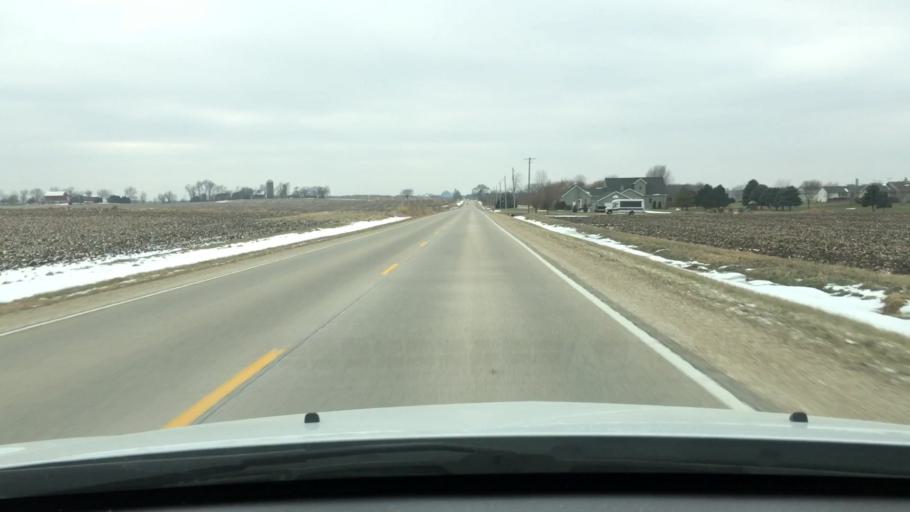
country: US
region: Illinois
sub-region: Ogle County
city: Rochelle
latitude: 41.8479
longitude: -88.9693
